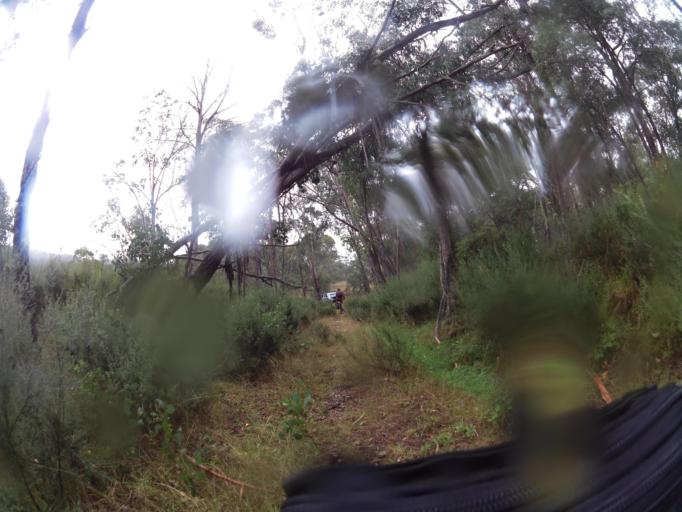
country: AU
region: New South Wales
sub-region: Greater Hume Shire
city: Holbrook
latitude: -36.2328
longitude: 147.5994
